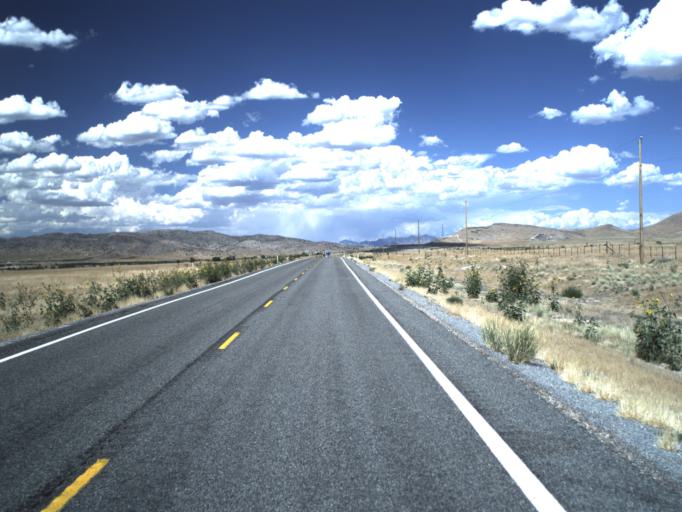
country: US
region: Utah
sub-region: Millard County
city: Delta
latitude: 39.6182
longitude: -112.3159
